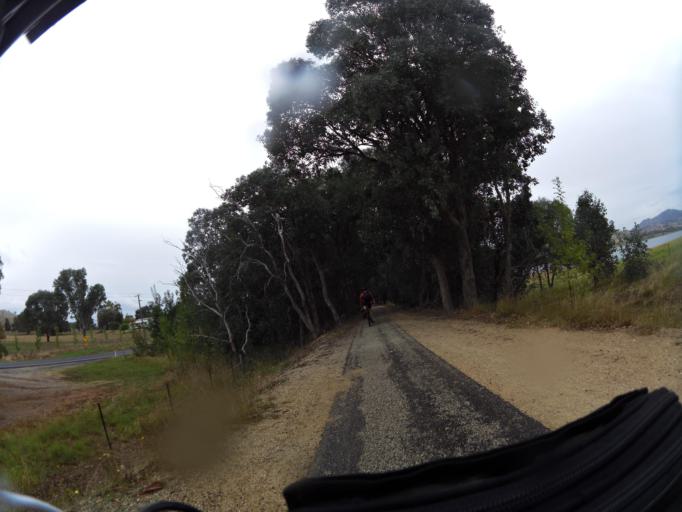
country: AU
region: New South Wales
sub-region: Albury Municipality
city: East Albury
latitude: -36.2308
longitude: 147.1000
